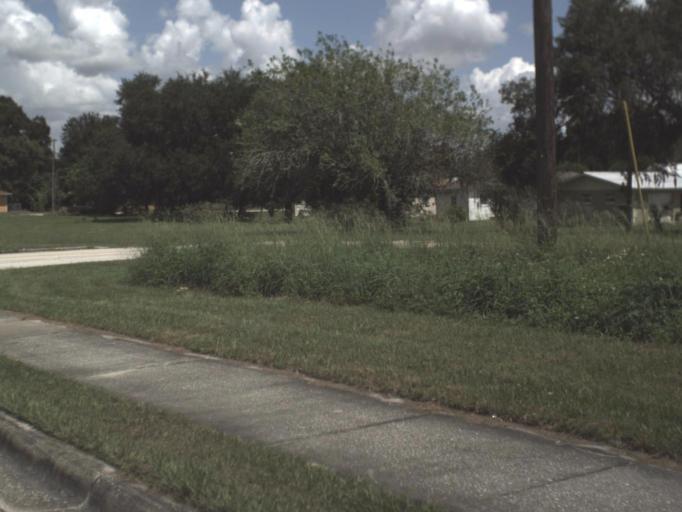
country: US
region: Florida
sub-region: Polk County
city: Bartow
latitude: 27.8920
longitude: -81.8282
